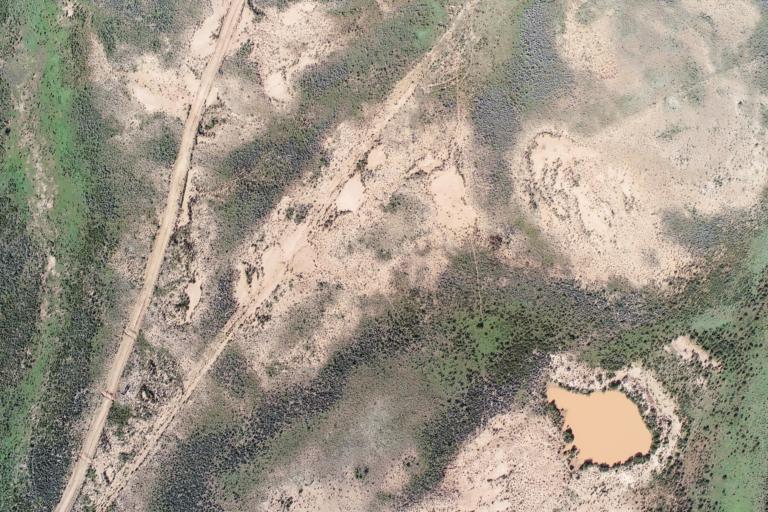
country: BO
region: La Paz
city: Curahuara de Carangas
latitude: -17.3034
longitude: -68.5114
